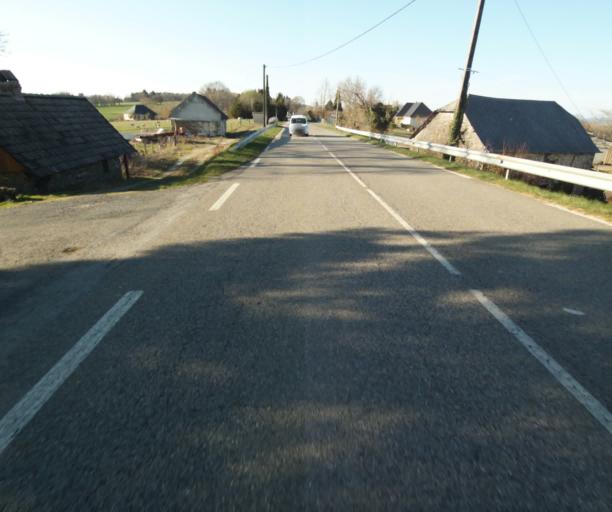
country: FR
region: Limousin
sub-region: Departement de la Correze
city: Seilhac
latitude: 45.3758
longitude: 1.7245
